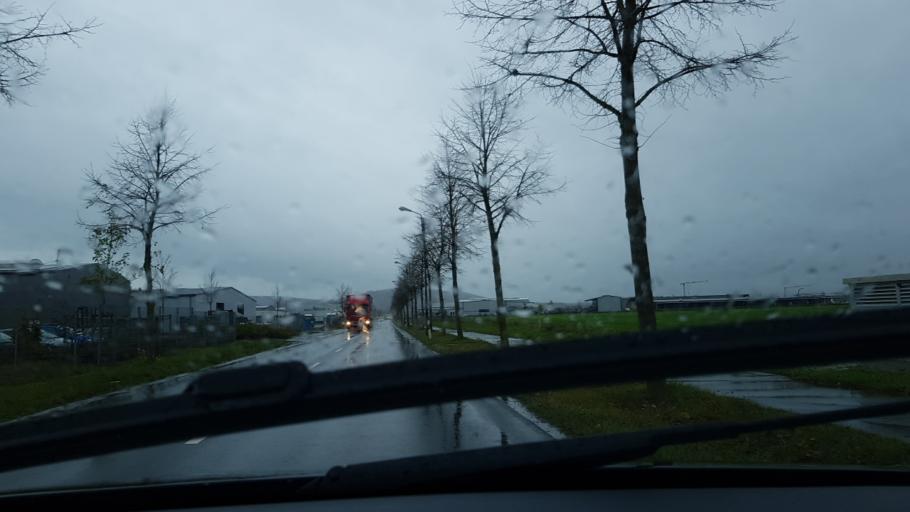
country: DE
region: Rheinland-Pfalz
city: Platten
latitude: 49.9721
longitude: 6.9516
